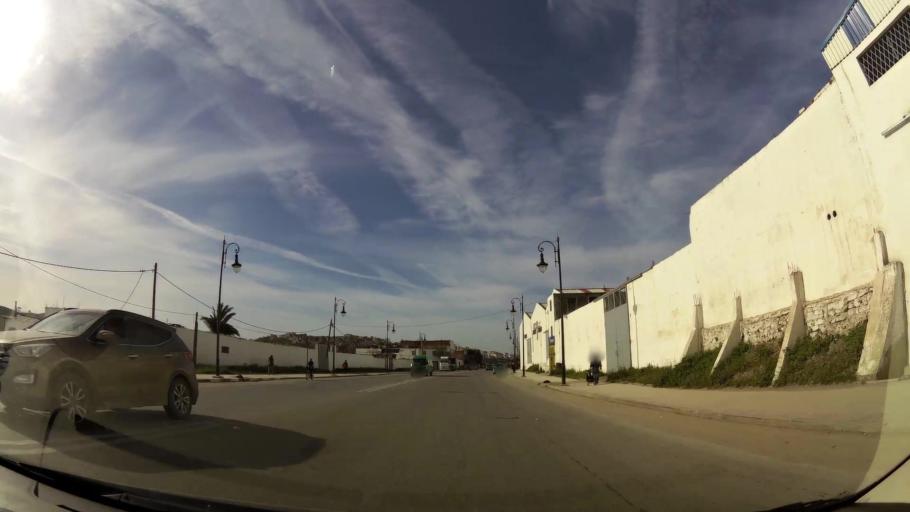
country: MA
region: Tanger-Tetouan
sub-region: Tanger-Assilah
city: Tangier
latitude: 35.7628
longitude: -5.7830
